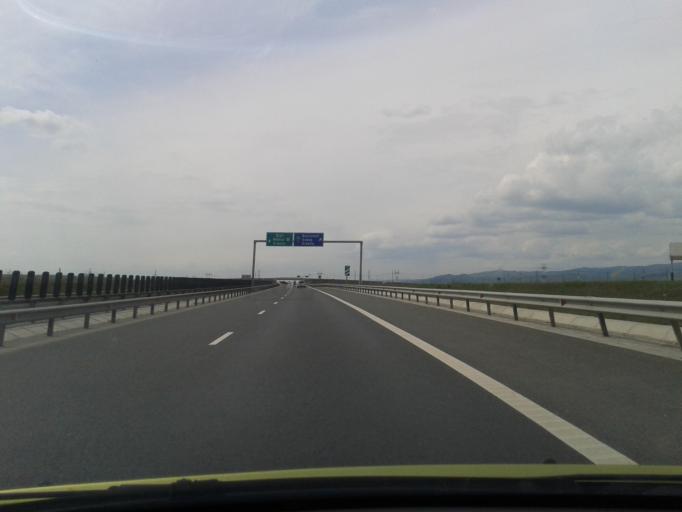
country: RO
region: Alba
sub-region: Municipiul Sebes
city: Lancram
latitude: 45.9804
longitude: 23.5351
